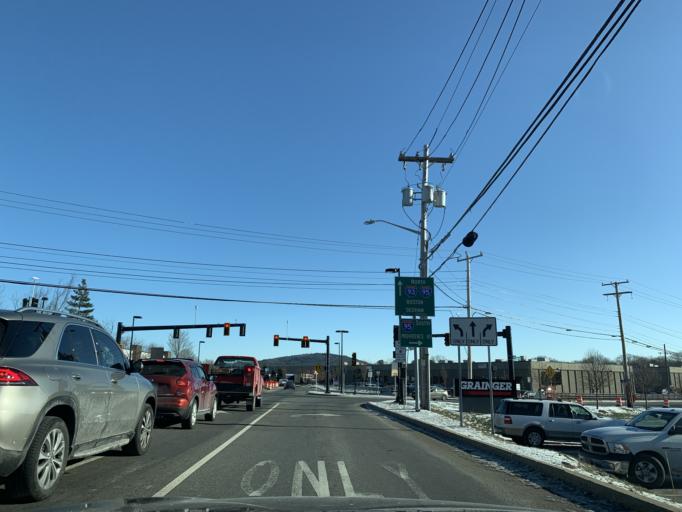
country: US
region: Massachusetts
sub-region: Norfolk County
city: Norwood
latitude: 42.1983
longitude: -71.1579
